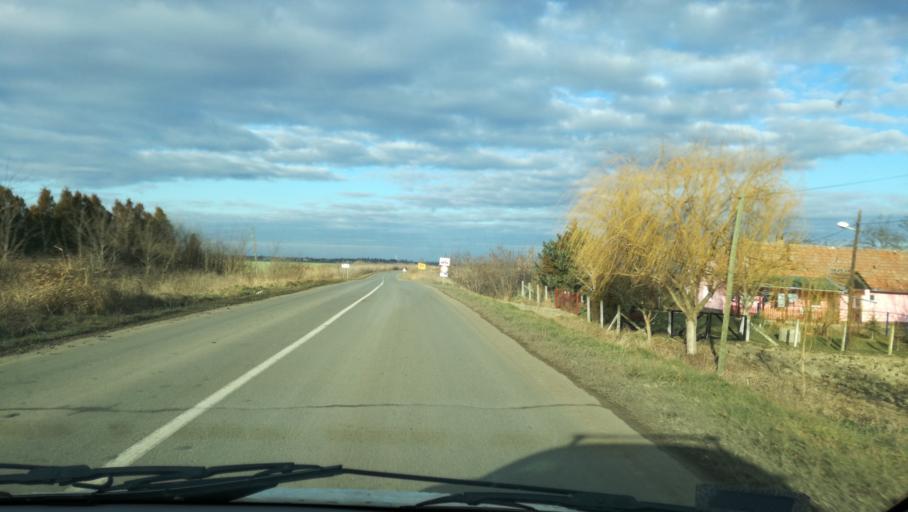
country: RS
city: Tiszahegyes
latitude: 45.8268
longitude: 20.3068
